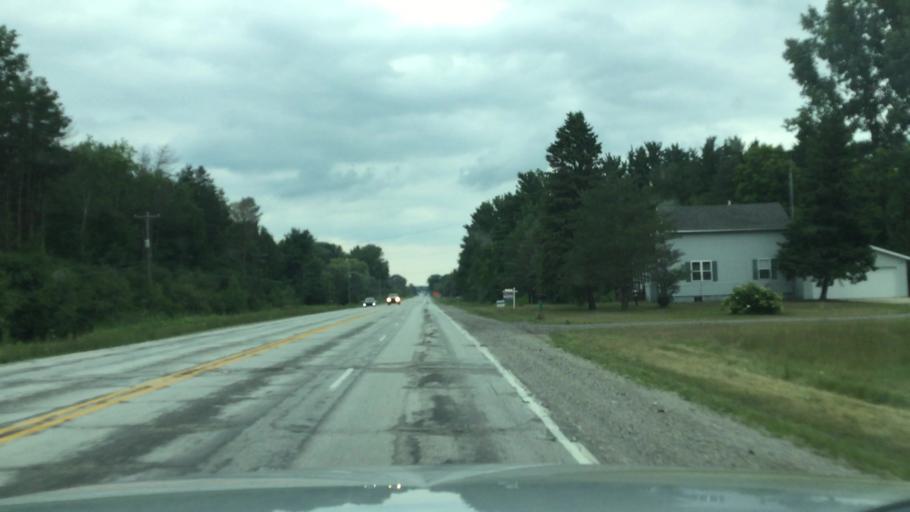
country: US
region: Michigan
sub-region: Saginaw County
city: Birch Run
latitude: 43.3144
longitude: -83.8178
